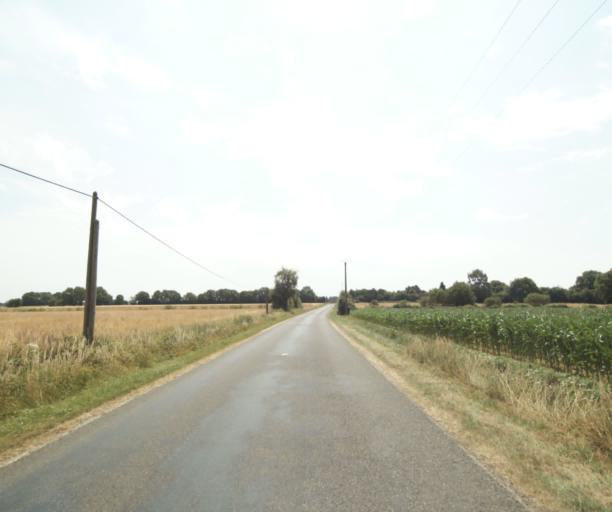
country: FR
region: Centre
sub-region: Departement d'Eure-et-Loir
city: La Bazoche-Gouet
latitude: 48.1815
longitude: 1.0118
